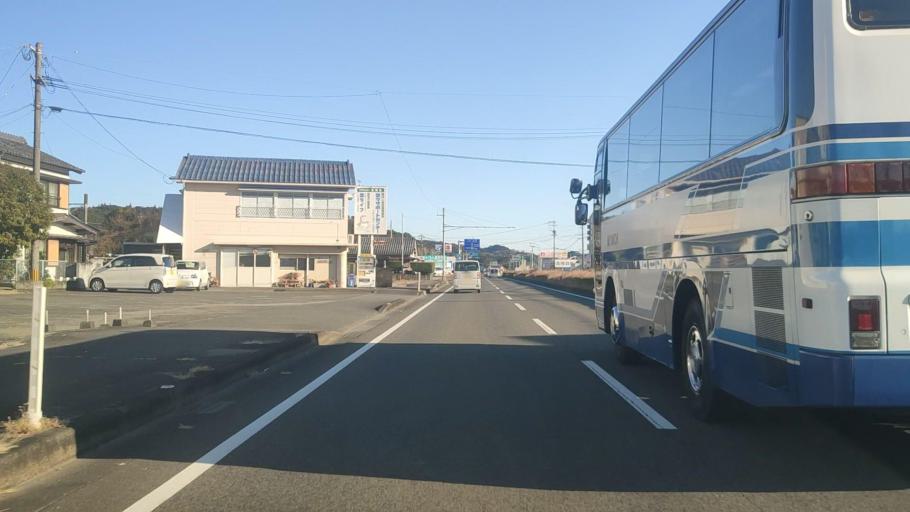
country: JP
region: Miyazaki
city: Nobeoka
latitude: 32.4774
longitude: 131.6547
